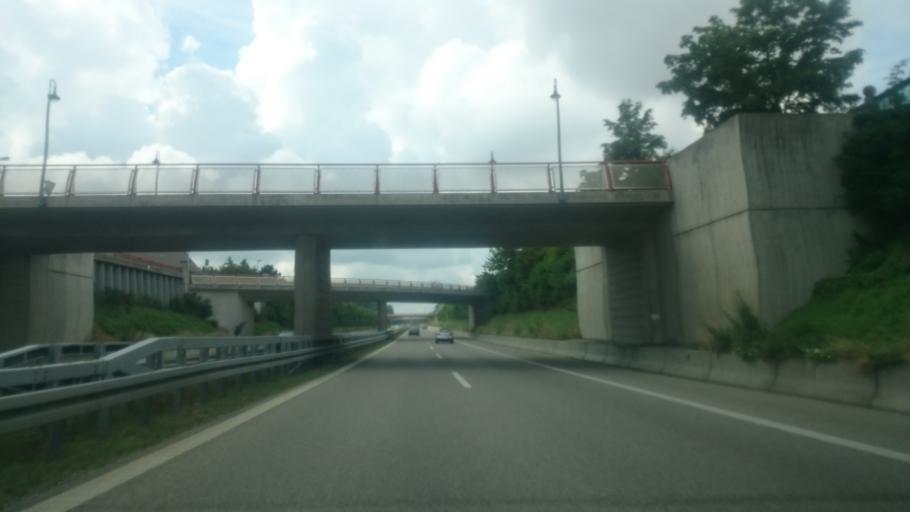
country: DE
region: Bavaria
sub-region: Swabia
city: Klosterlechfeld
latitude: 48.1864
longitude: 10.8464
